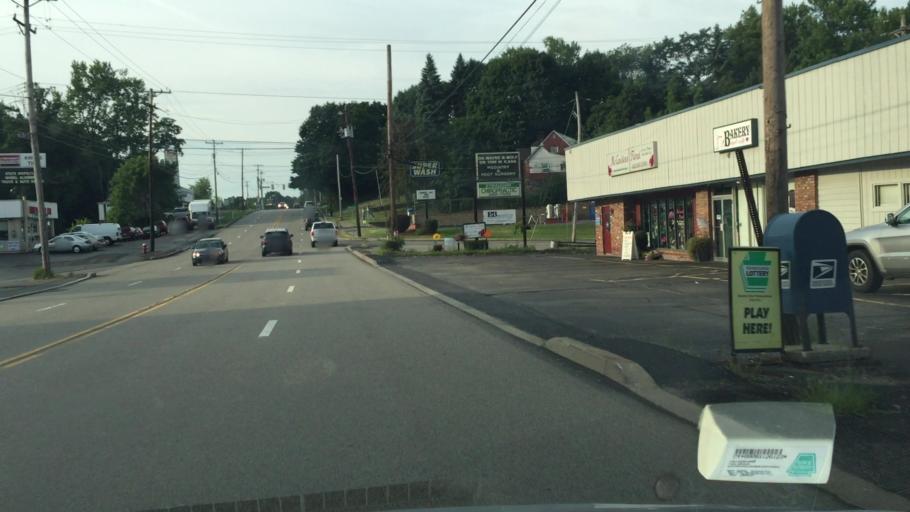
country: US
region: Pennsylvania
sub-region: Allegheny County
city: West View
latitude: 40.5548
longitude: -80.0387
